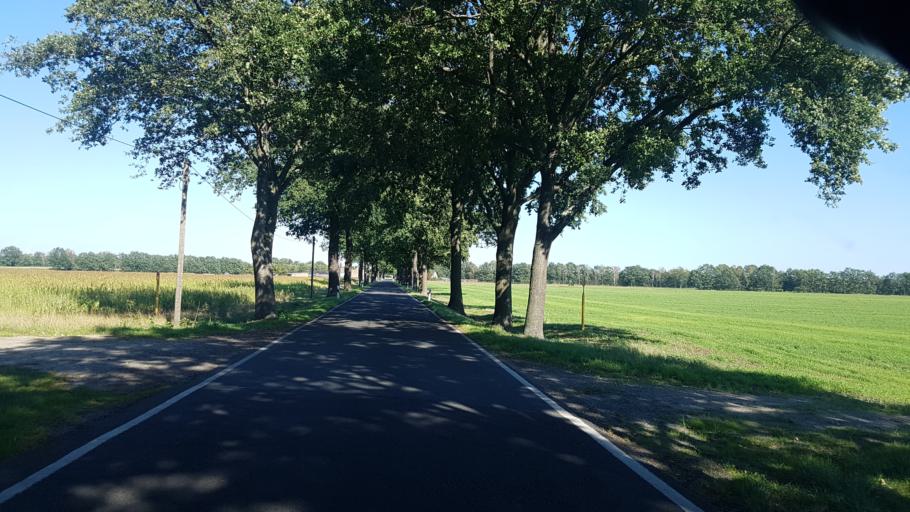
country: DE
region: Brandenburg
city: Schraden
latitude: 51.4298
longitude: 13.7096
